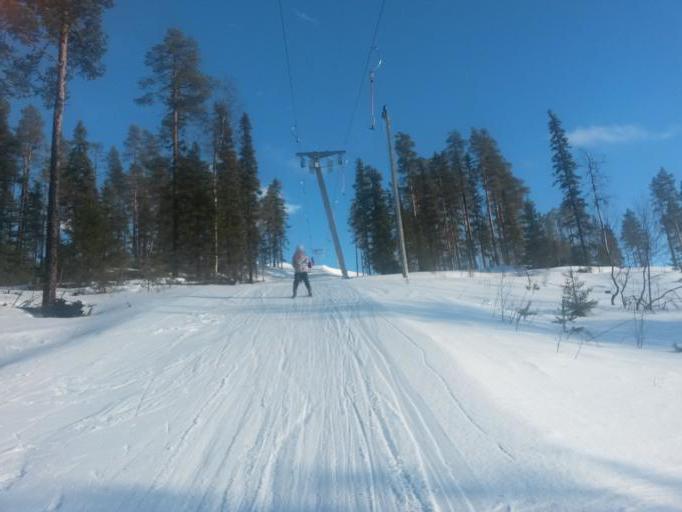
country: SE
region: Vaesterbotten
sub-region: Mala Kommun
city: Mala
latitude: 65.1788
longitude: 18.7632
